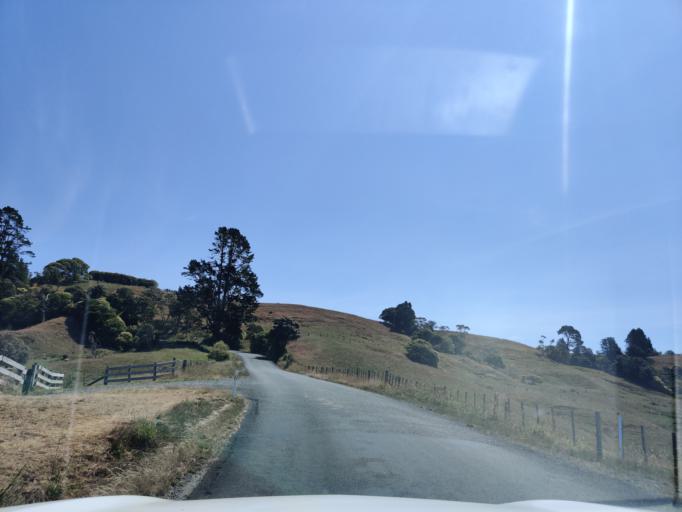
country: NZ
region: Auckland
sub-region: Auckland
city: Red Hill
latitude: -37.0633
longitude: 175.0789
